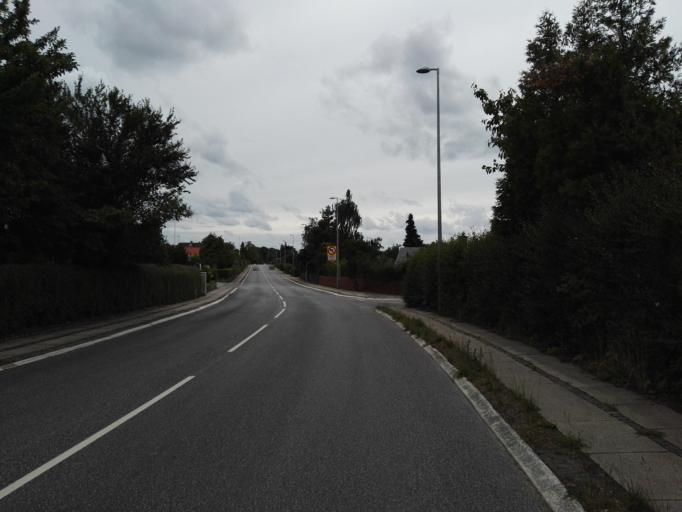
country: DK
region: Capital Region
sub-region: Egedal Kommune
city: Stenlose
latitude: 55.7736
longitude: 12.2050
